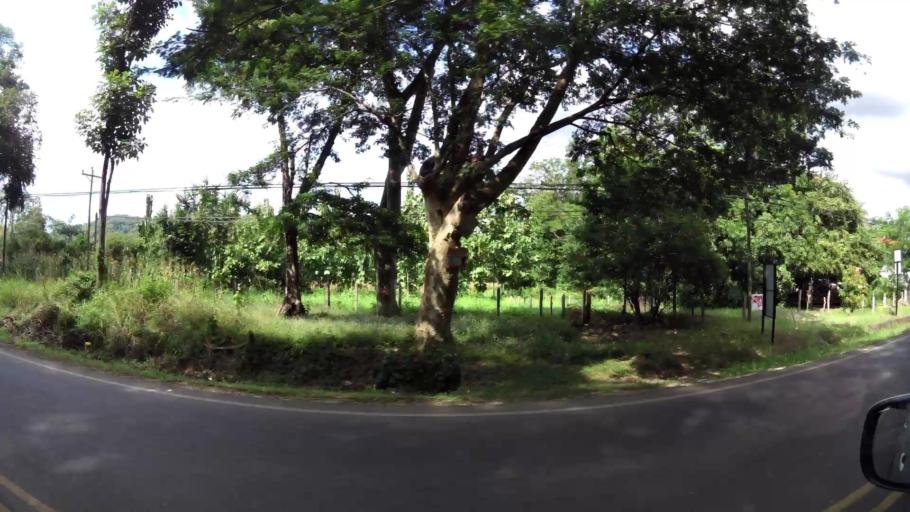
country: CR
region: Guanacaste
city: Hojancha
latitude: 10.1101
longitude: -85.3479
